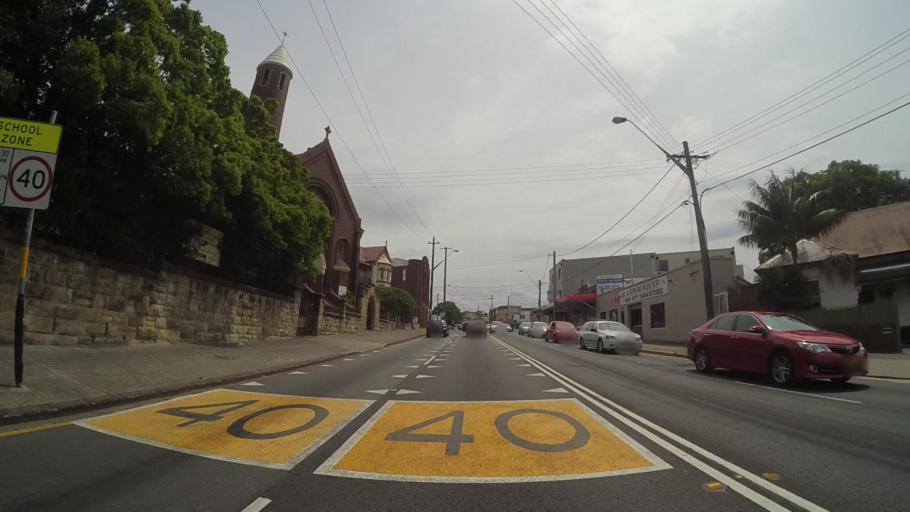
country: AU
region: New South Wales
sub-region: Rockdale
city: Arncliffe
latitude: -33.9392
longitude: 151.1472
